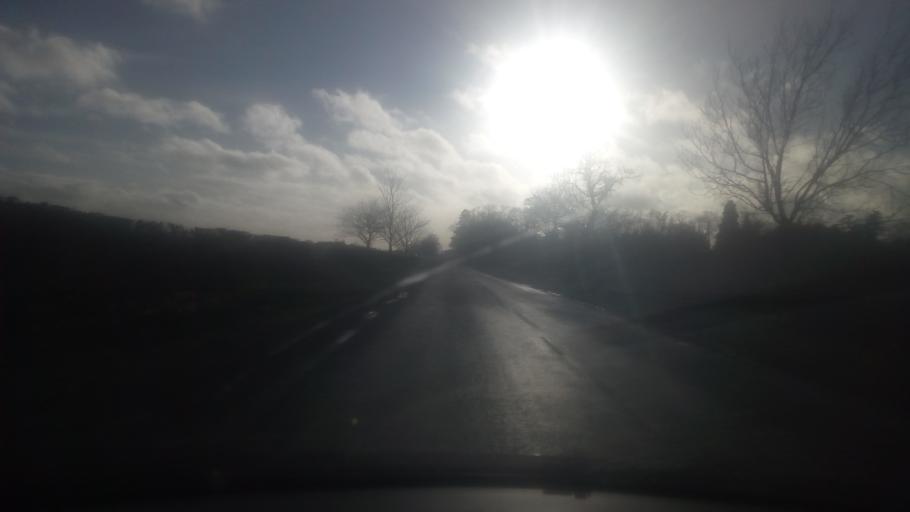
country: GB
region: Scotland
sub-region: The Scottish Borders
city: Coldstream
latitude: 55.6972
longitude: -2.3195
